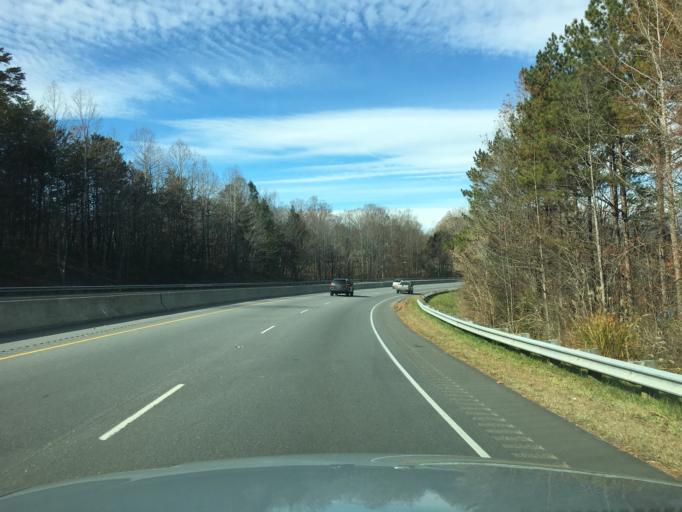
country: US
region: North Carolina
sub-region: McDowell County
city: Marion
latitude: 35.6788
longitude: -82.0263
